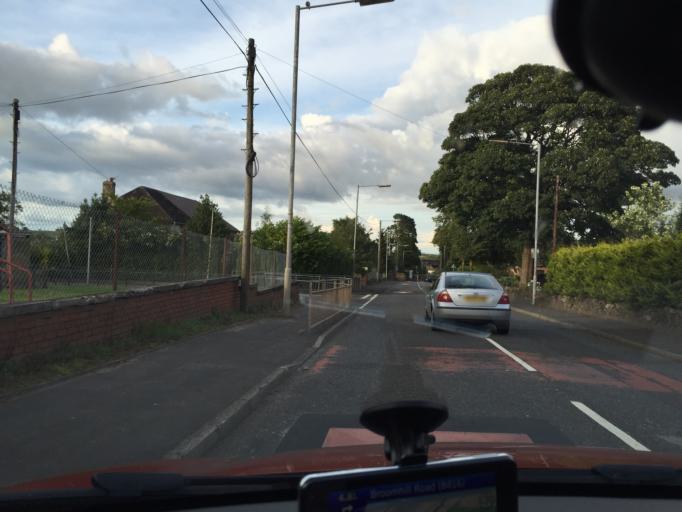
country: GB
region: Scotland
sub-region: North Lanarkshire
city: Cumbernauld
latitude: 55.9784
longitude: -3.9495
